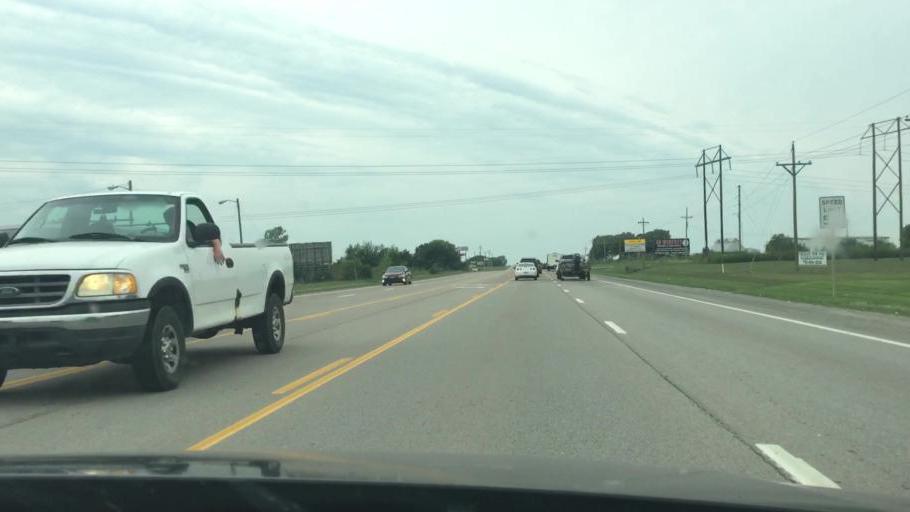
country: US
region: Missouri
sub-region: Pettis County
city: Sedalia
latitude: 38.7157
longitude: -93.2850
